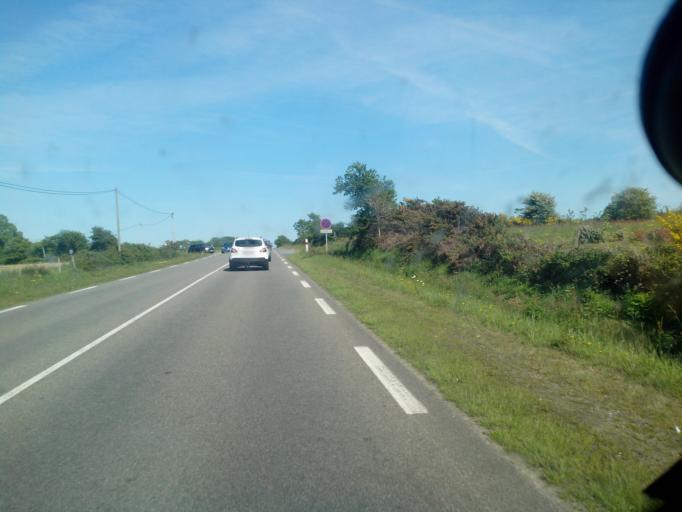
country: FR
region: Pays de la Loire
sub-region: Departement de la Loire-Atlantique
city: La Bernerie-en-Retz
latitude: 47.1119
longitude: -2.0181
